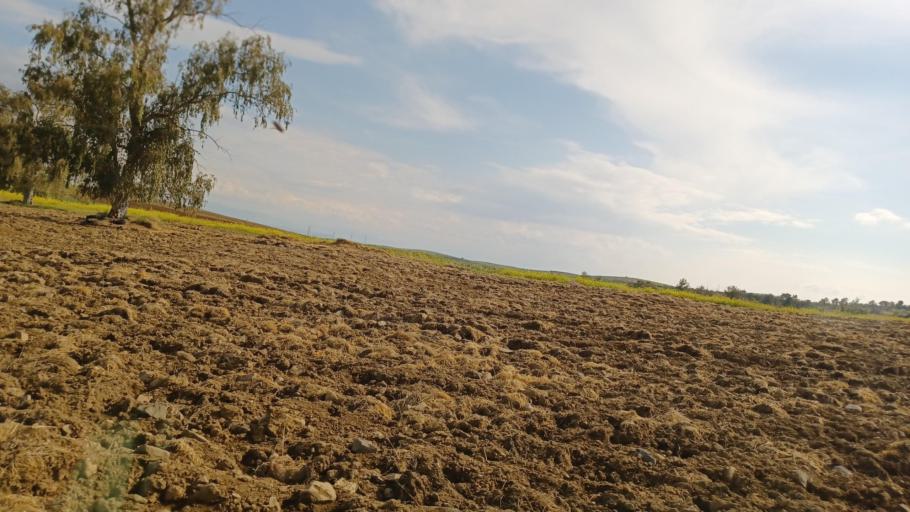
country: CY
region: Lefkosia
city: Kakopetria
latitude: 35.0772
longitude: 32.9534
